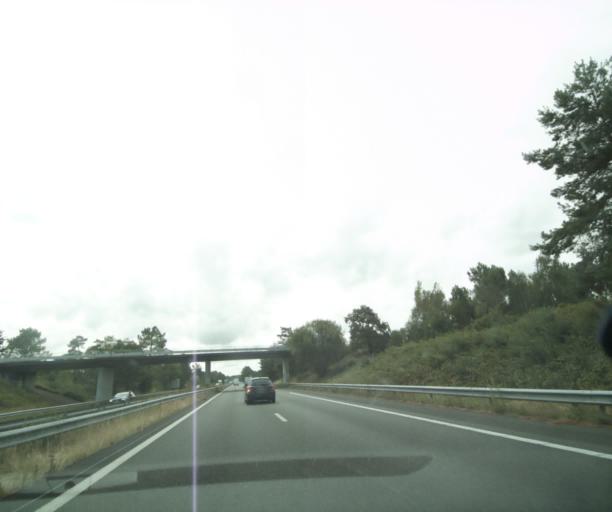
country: FR
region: Poitou-Charentes
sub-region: Departement de la Charente-Maritime
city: Saint-Genis-de-Saintonge
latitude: 45.4545
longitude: -0.6154
